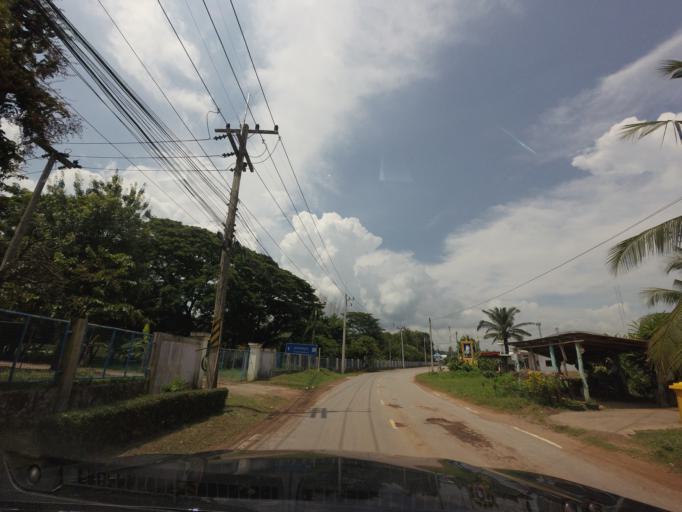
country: TH
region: Khon Kaen
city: Wiang Kao
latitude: 16.6772
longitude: 102.2924
